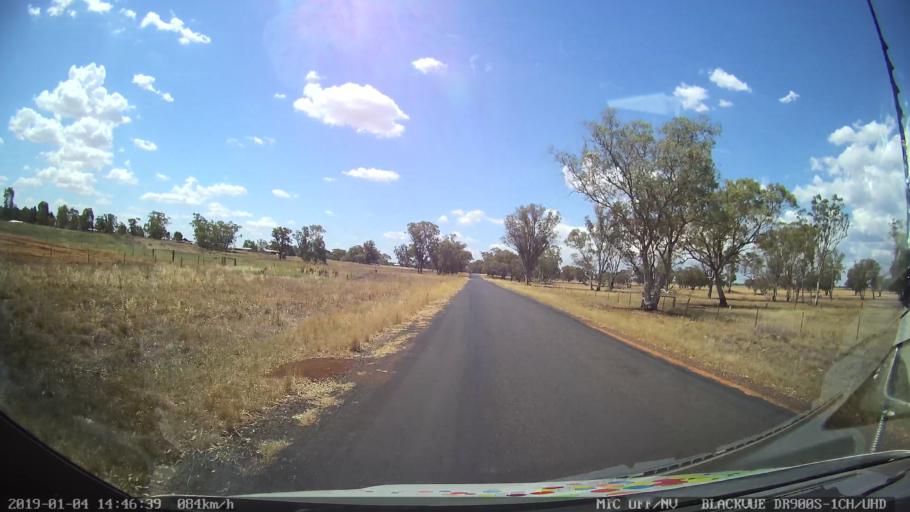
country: AU
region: New South Wales
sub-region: Dubbo Municipality
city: Dubbo
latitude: -32.0789
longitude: 148.6586
